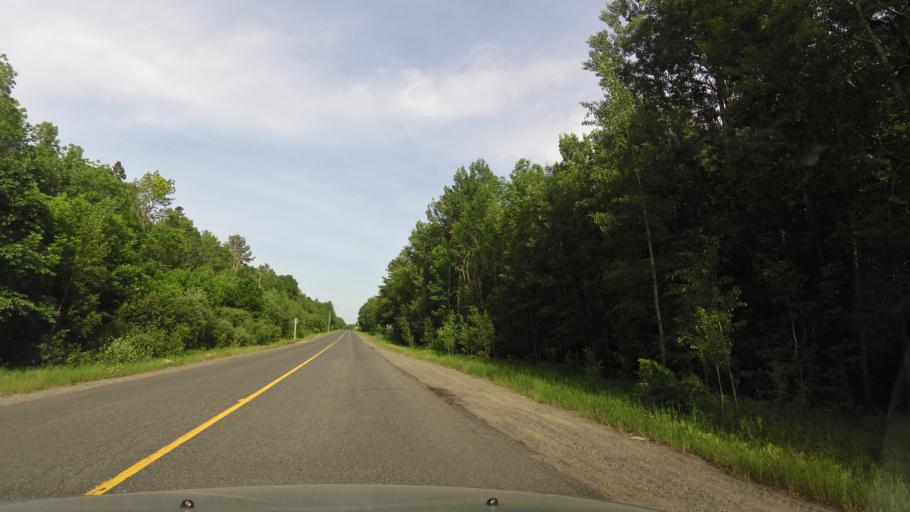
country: CA
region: Ontario
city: Greater Sudbury
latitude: 45.9134
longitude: -80.5688
